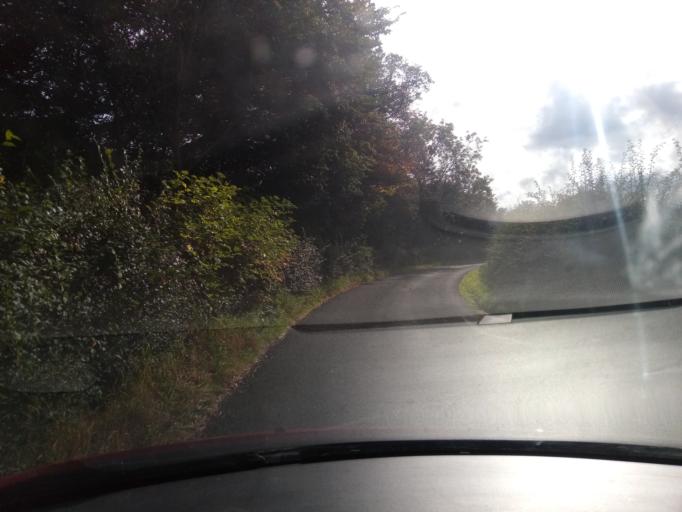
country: GB
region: Scotland
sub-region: The Scottish Borders
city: Kelso
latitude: 55.4862
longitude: -2.3478
